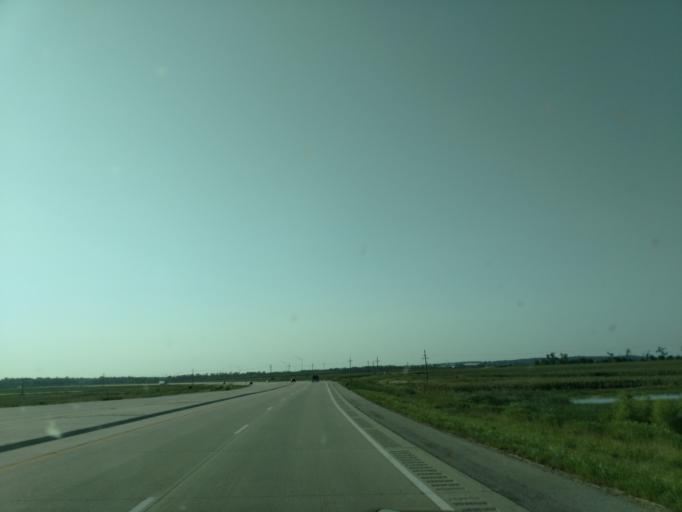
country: US
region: Nebraska
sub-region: Sarpy County
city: Offutt Air Force Base
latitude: 41.0735
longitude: -95.8875
